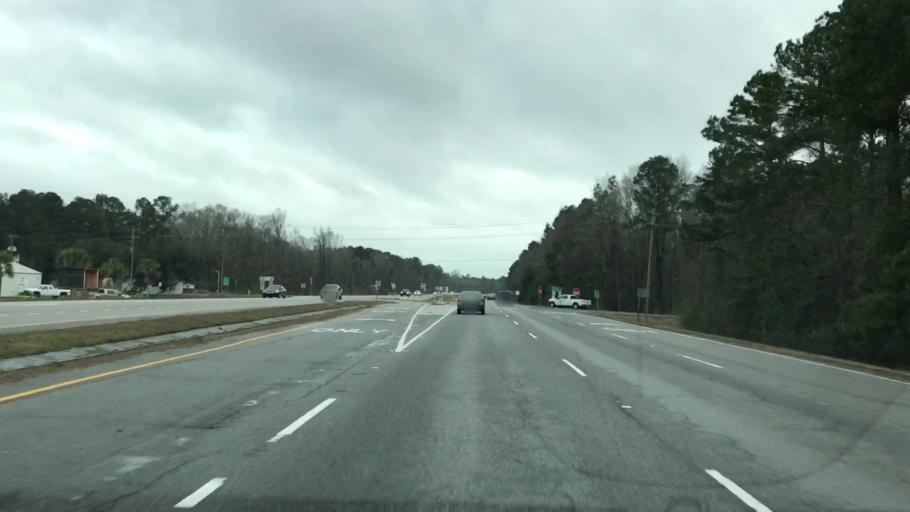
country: US
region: South Carolina
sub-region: Berkeley County
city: Moncks Corner
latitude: 33.1268
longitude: -80.0298
